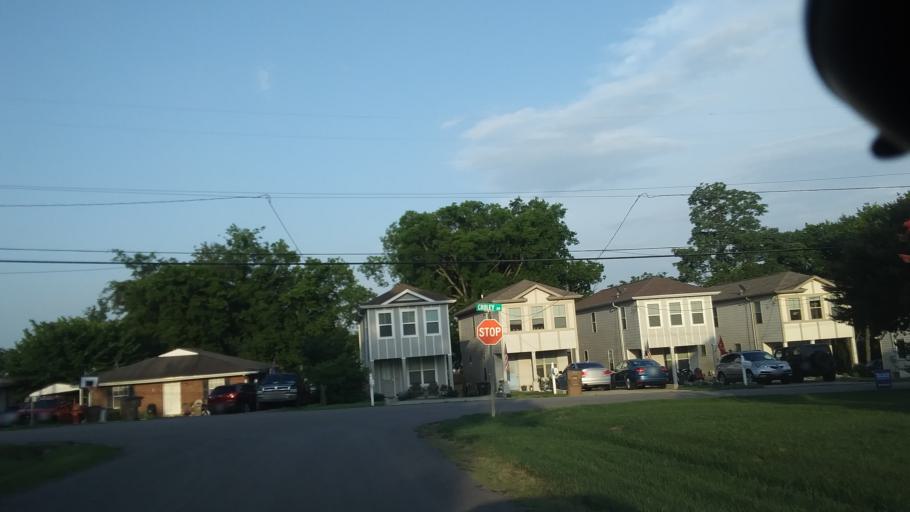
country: US
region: Tennessee
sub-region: Davidson County
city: Belle Meade
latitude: 36.1593
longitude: -86.8748
